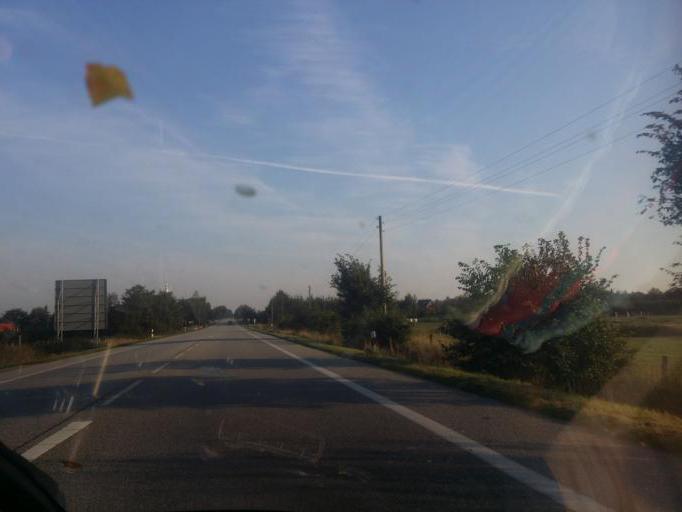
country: DE
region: Schleswig-Holstein
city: Bredstedt
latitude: 54.6333
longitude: 8.9533
